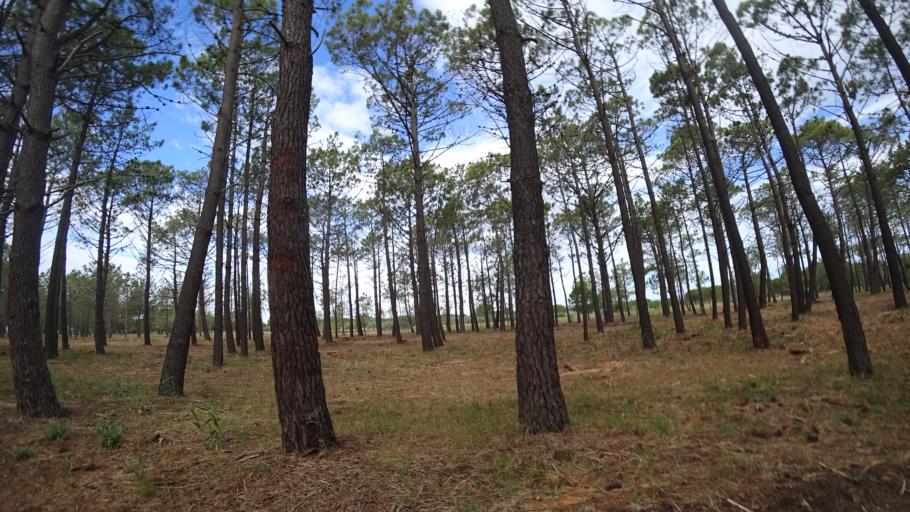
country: FR
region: Languedoc-Roussillon
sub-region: Departement des Pyrenees-Orientales
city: Le Barcares
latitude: 42.8184
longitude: 3.0339
